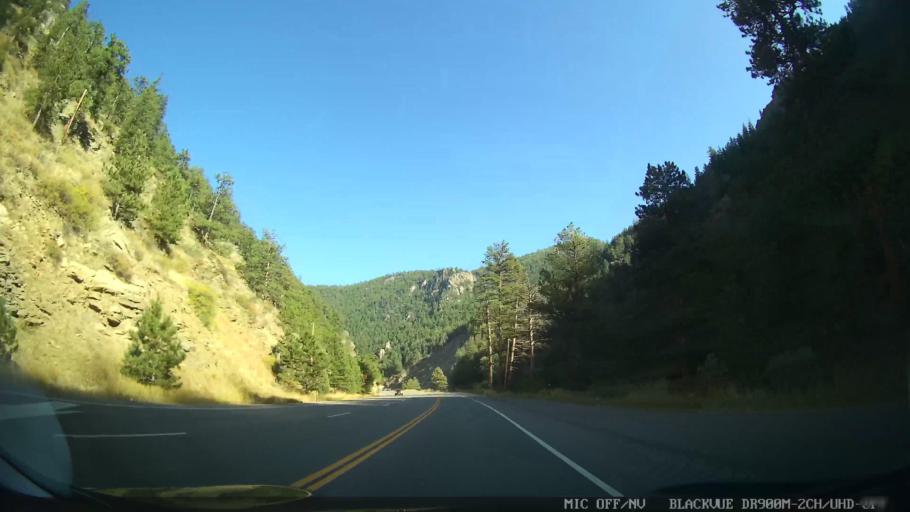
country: US
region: Colorado
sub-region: Larimer County
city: Estes Park
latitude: 40.4099
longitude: -105.3872
